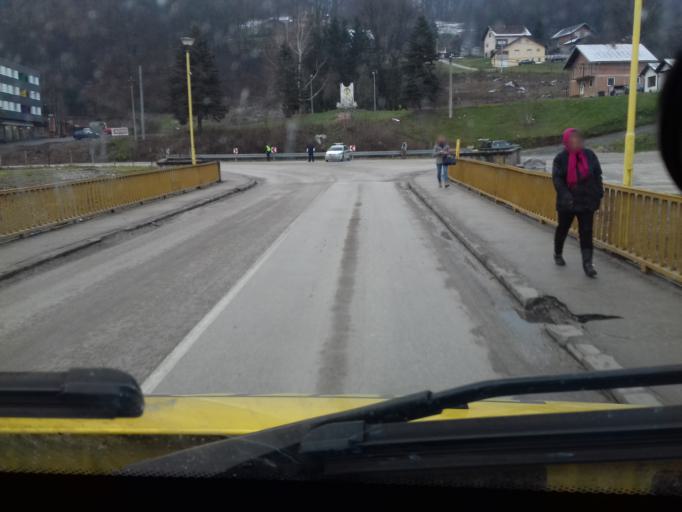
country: BA
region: Federation of Bosnia and Herzegovina
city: Zepce
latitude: 44.4228
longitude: 18.0408
